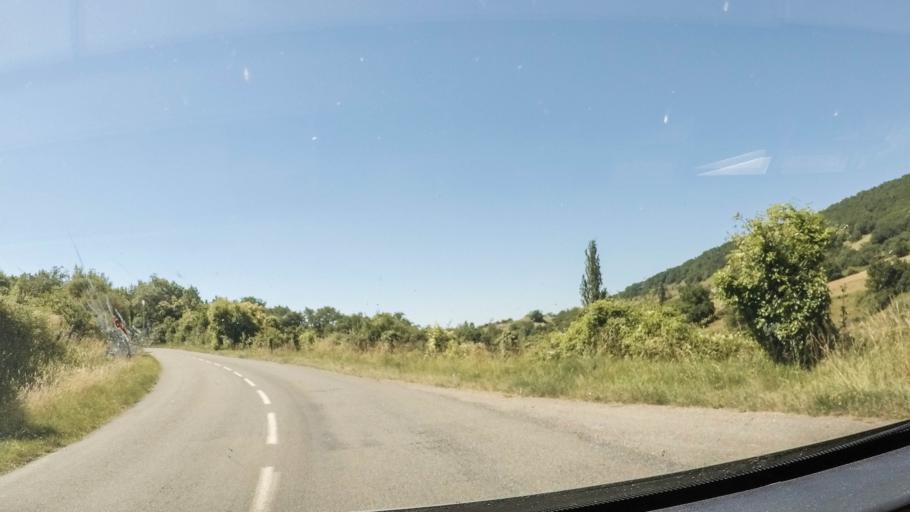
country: FR
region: Midi-Pyrenees
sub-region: Departement de l'Aveyron
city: Saint-Christophe-Vallon
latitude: 44.4665
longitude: 2.3751
